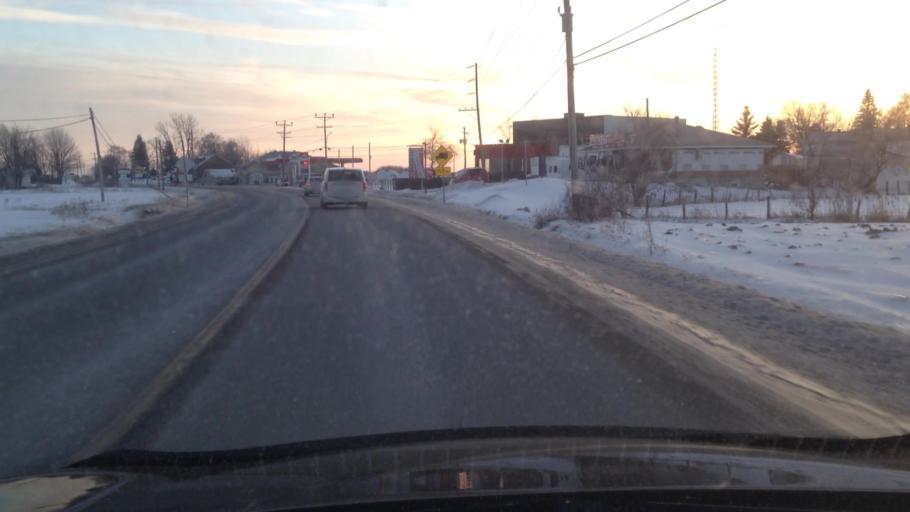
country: CA
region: Quebec
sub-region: Lanaudiere
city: Saint-Lin-Laurentides
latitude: 45.8903
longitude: -73.7575
